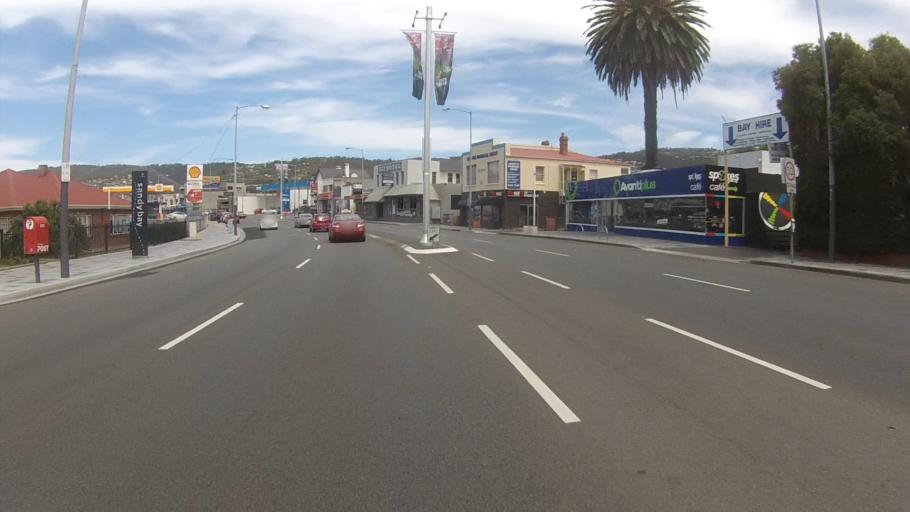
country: AU
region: Tasmania
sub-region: Hobart
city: Sandy Bay
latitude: -42.8929
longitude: 147.3259
